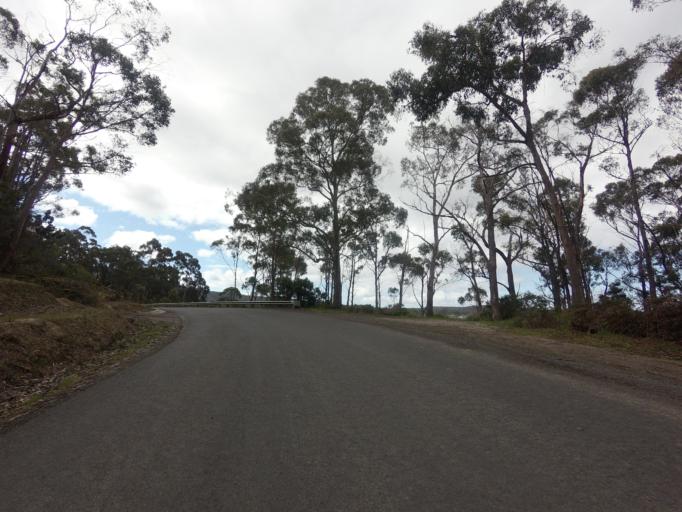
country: AU
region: Tasmania
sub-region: Huon Valley
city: Geeveston
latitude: -43.4347
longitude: 146.9665
